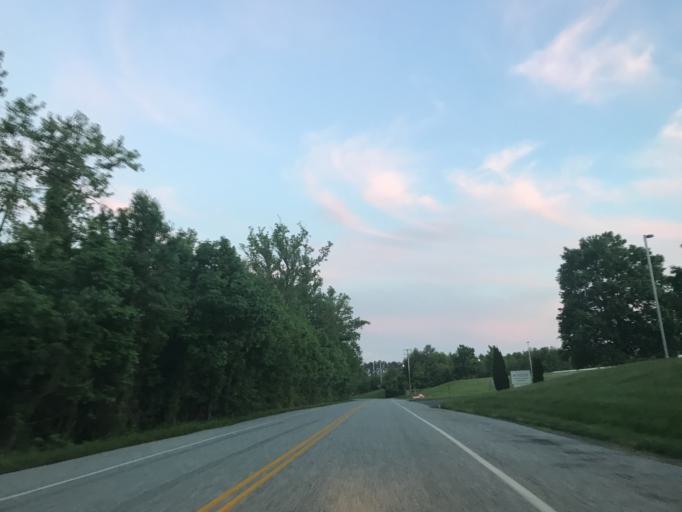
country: US
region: Maryland
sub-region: Harford County
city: Joppatowne
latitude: 39.4479
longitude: -76.3208
